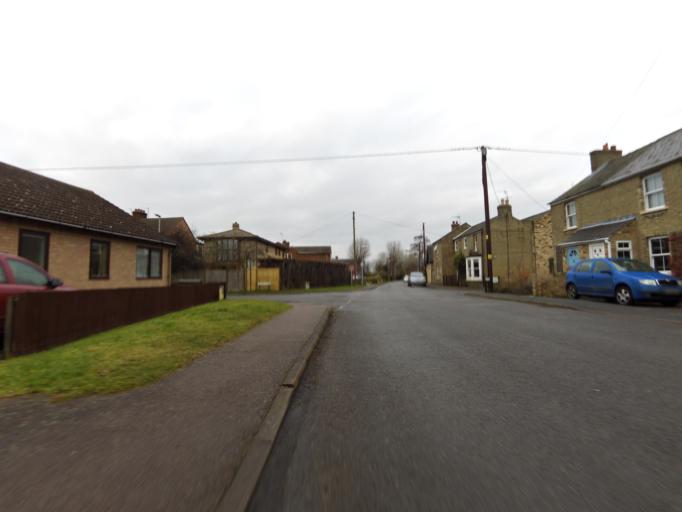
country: GB
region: England
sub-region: Cambridgeshire
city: Waterbeach
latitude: 52.2674
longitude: 0.1935
